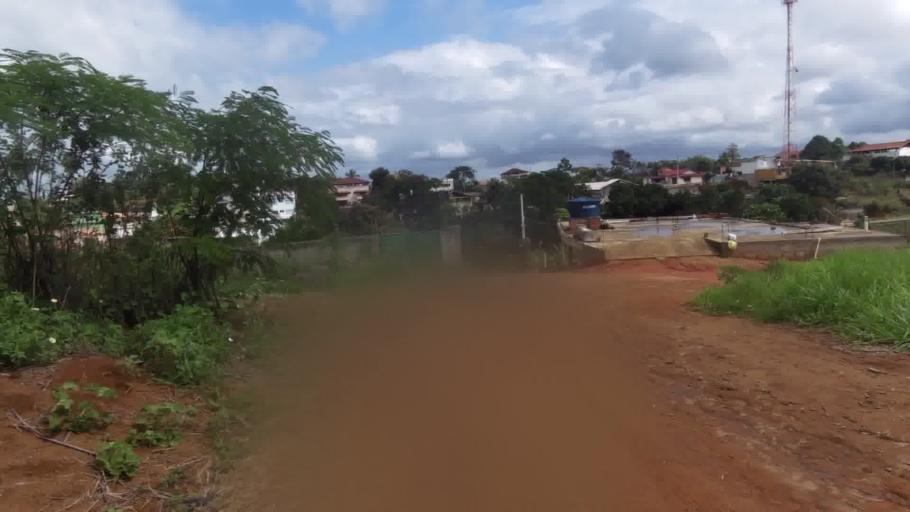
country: BR
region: Espirito Santo
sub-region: Piuma
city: Piuma
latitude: -20.8283
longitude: -40.6956
